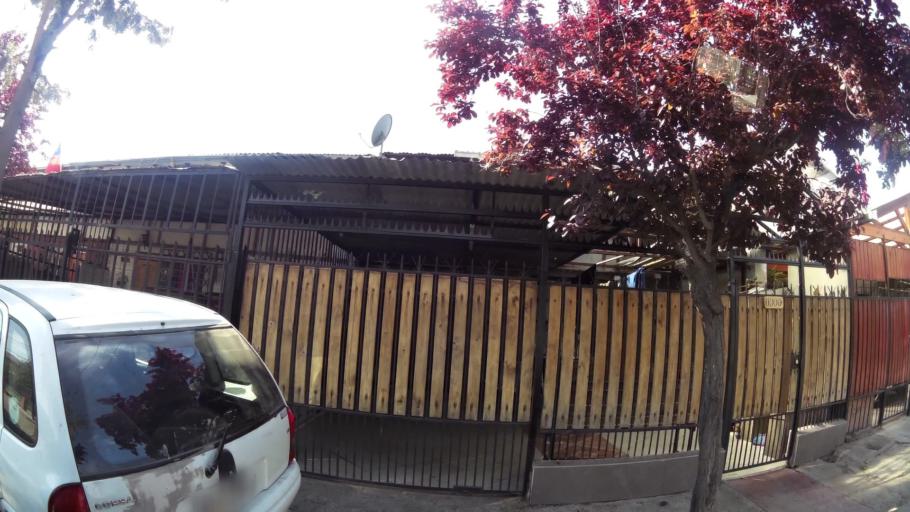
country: CL
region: Santiago Metropolitan
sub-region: Provincia de Santiago
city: La Pintana
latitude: -33.5631
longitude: -70.6475
